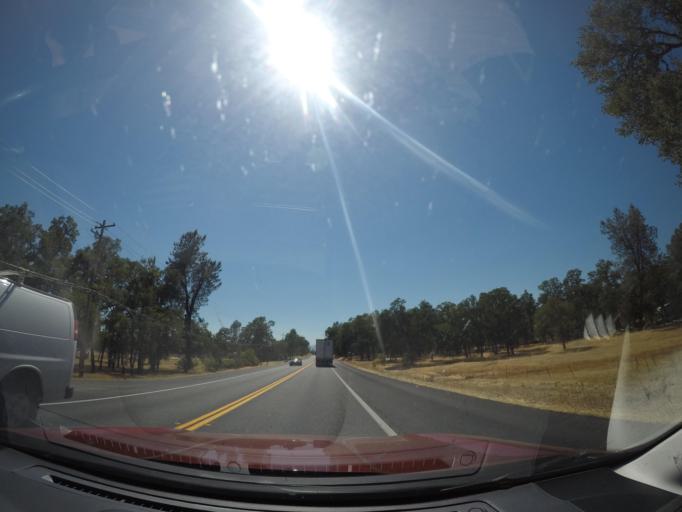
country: US
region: California
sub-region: Shasta County
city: Bella Vista
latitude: 40.6321
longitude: -122.2659
